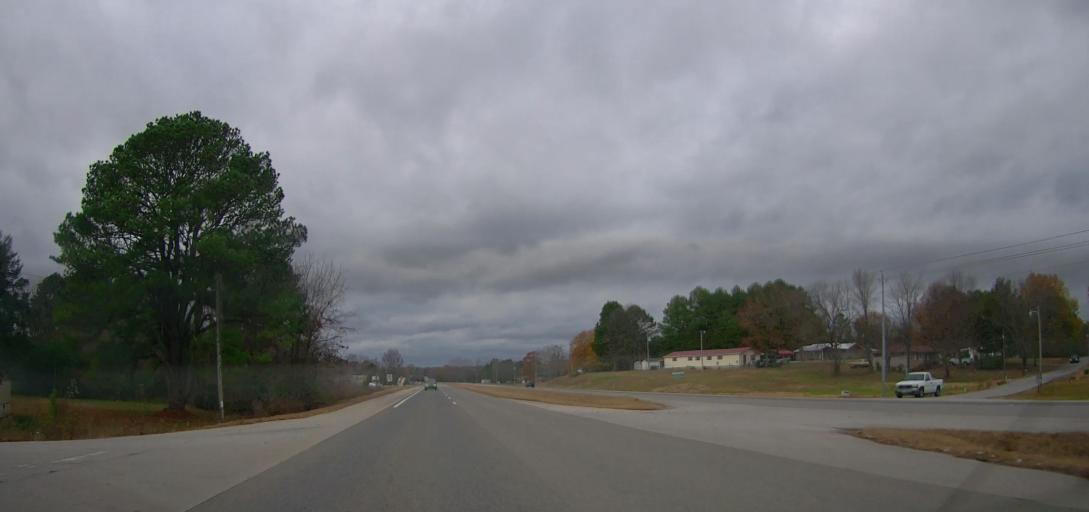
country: US
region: Alabama
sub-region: Colbert County
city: Cherokee
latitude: 34.7508
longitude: -87.9624
